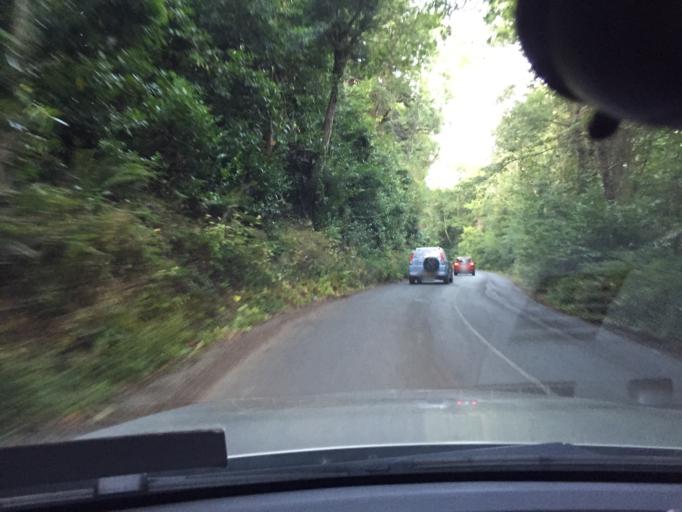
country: IE
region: Leinster
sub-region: Wicklow
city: Enniskerry
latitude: 53.1777
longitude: -6.1754
